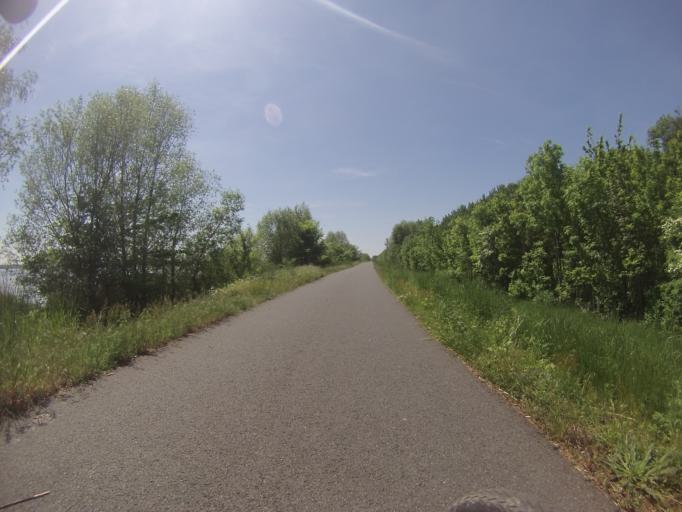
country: CZ
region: South Moravian
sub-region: Okres Breclav
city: Dolni Dunajovice
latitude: 48.9089
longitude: 16.6023
